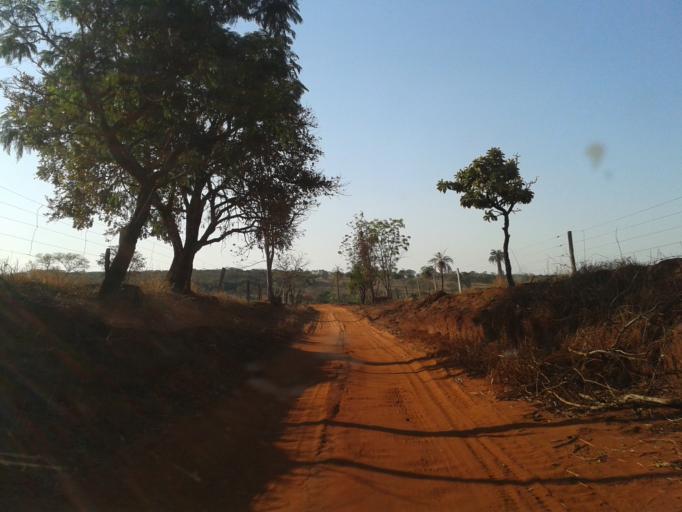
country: BR
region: Minas Gerais
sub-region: Ituiutaba
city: Ituiutaba
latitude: -19.2497
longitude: -49.5781
